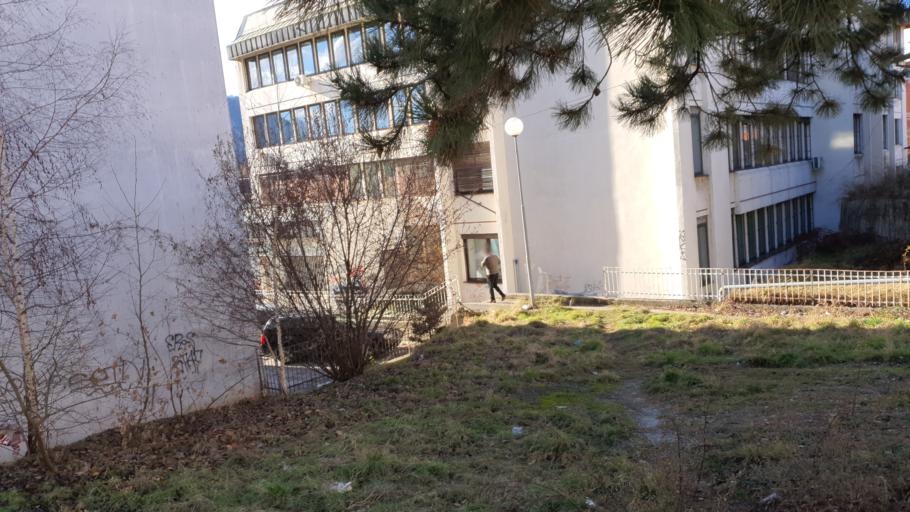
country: RS
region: Central Serbia
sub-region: Zlatiborski Okrug
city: Uzice
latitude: 43.8589
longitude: 19.8412
